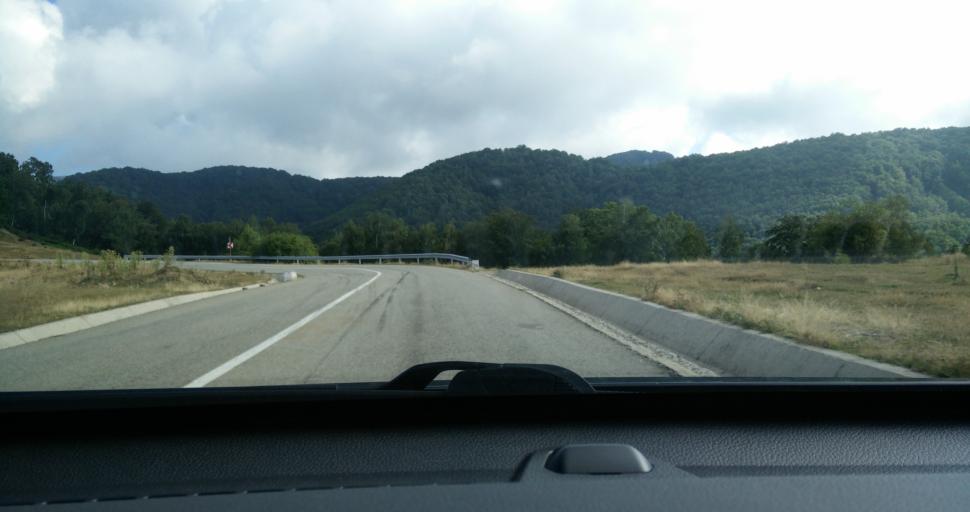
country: RO
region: Gorj
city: Novaci-Straini
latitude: 45.2177
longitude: 23.6987
